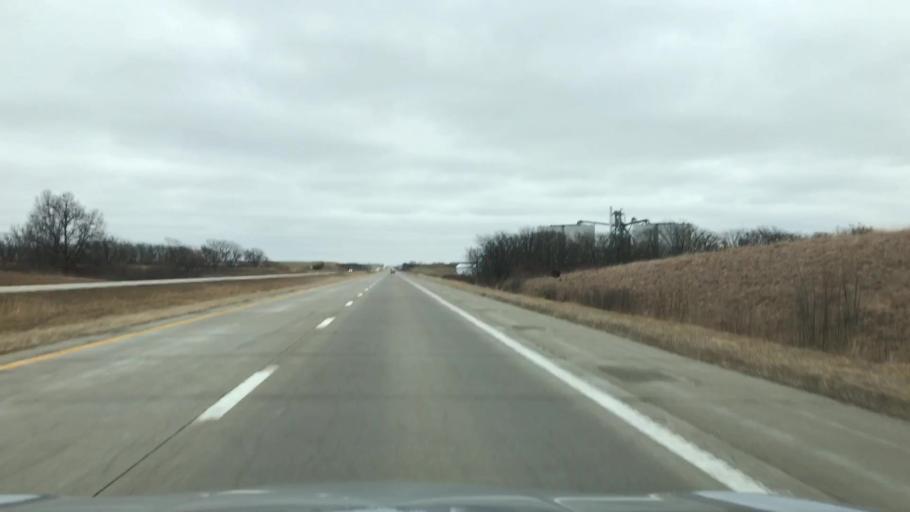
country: US
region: Missouri
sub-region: Caldwell County
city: Hamilton
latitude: 39.7353
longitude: -93.9145
